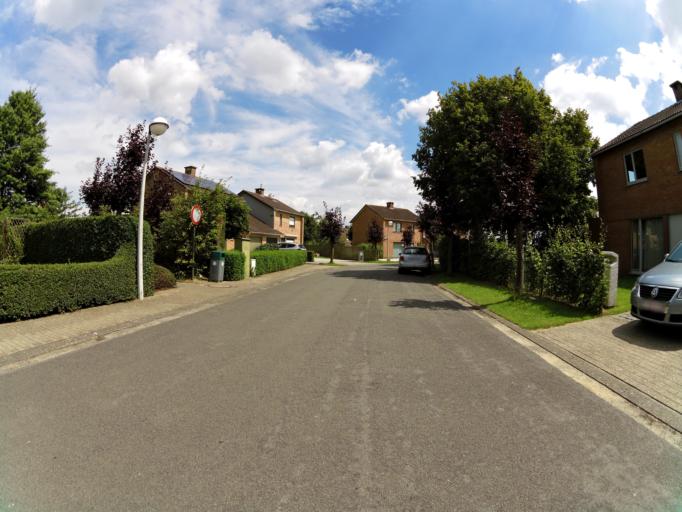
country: BE
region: Flanders
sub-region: Provincie West-Vlaanderen
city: Gistel
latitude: 51.1733
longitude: 2.9389
